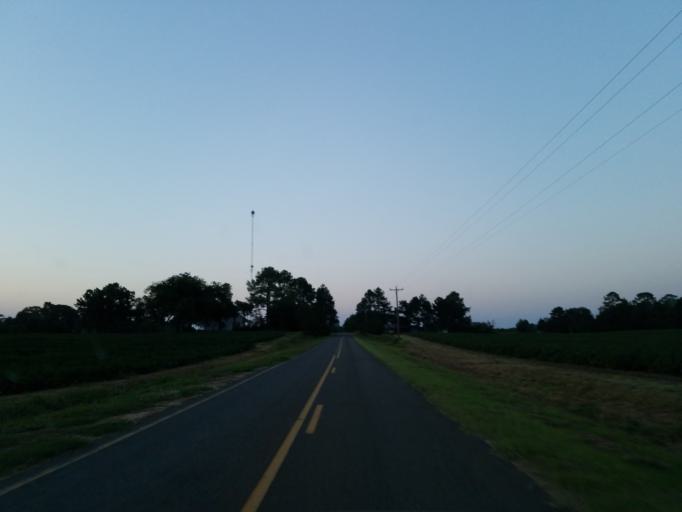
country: US
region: Georgia
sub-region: Dooly County
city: Unadilla
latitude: 32.2373
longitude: -83.7975
